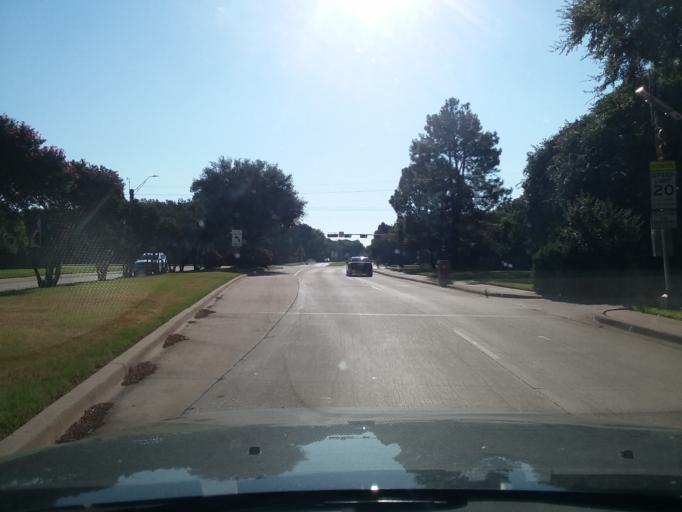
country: US
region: Texas
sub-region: Denton County
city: Highland Village
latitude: 33.0521
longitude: -97.0628
